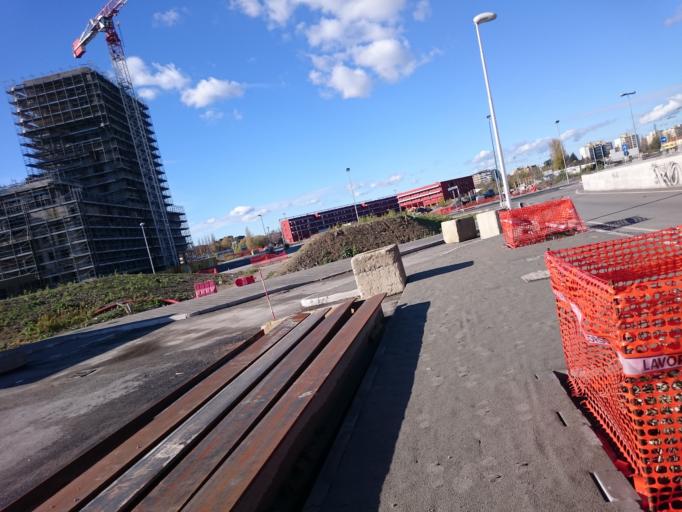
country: IT
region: Emilia-Romagna
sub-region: Provincia di Bologna
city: Bologna
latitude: 44.5131
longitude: 11.3399
